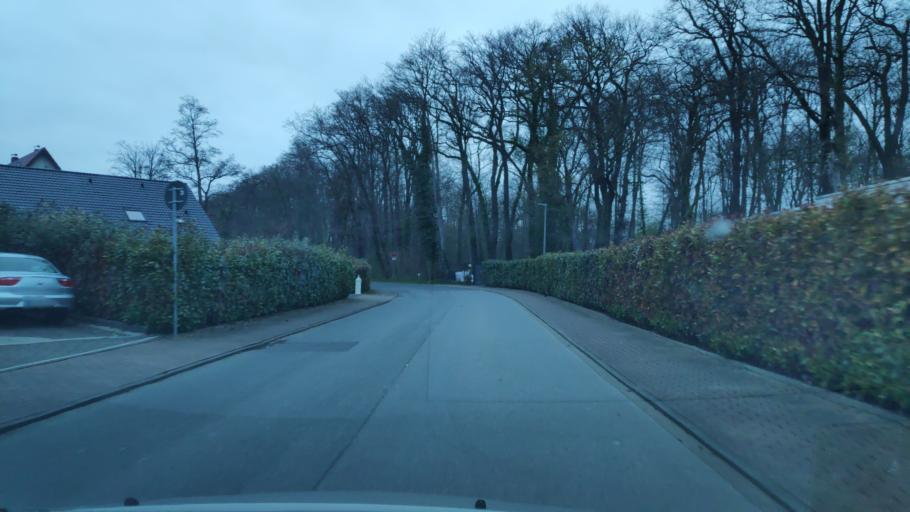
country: DE
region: North Rhine-Westphalia
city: Bad Oeynhausen
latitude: 52.2072
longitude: 8.7843
